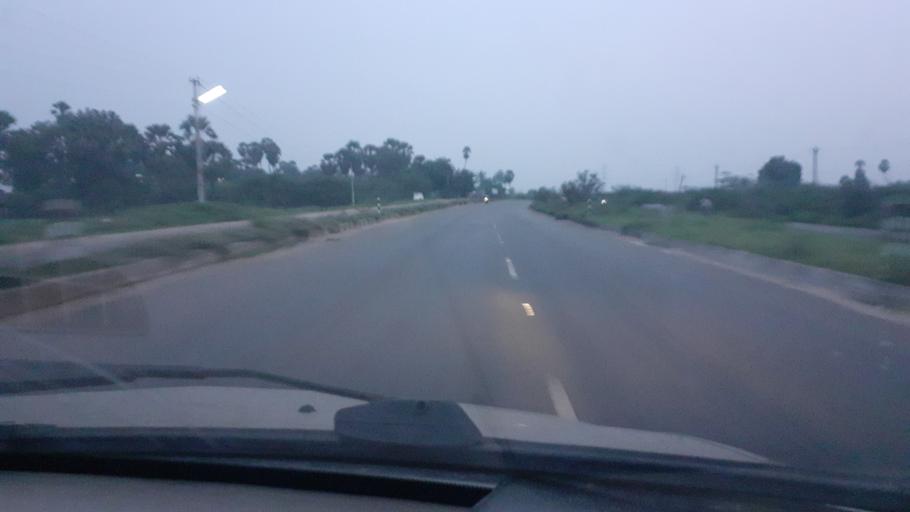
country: IN
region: Tamil Nadu
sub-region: Thoothukkudi
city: Srivaikuntam
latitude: 8.7096
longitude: 77.8213
